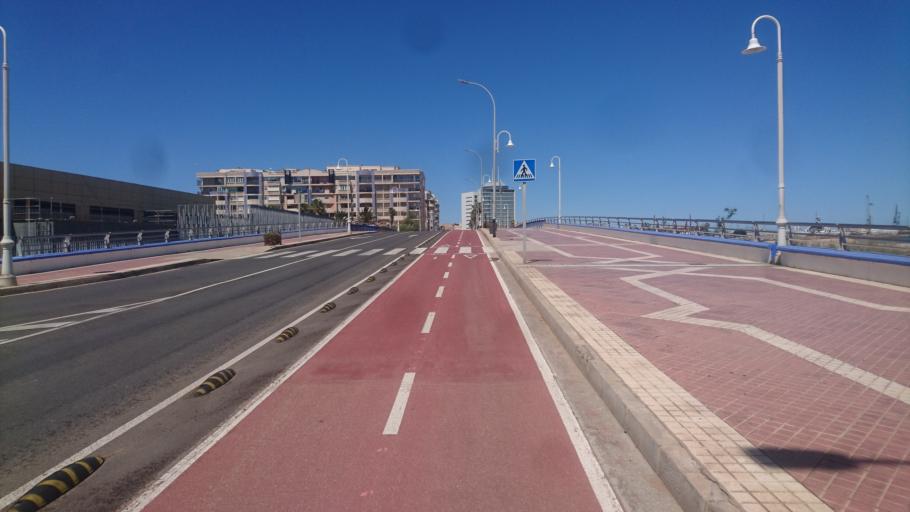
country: ES
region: Melilla
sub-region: Melilla
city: Melilla
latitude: 35.2852
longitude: -2.9388
